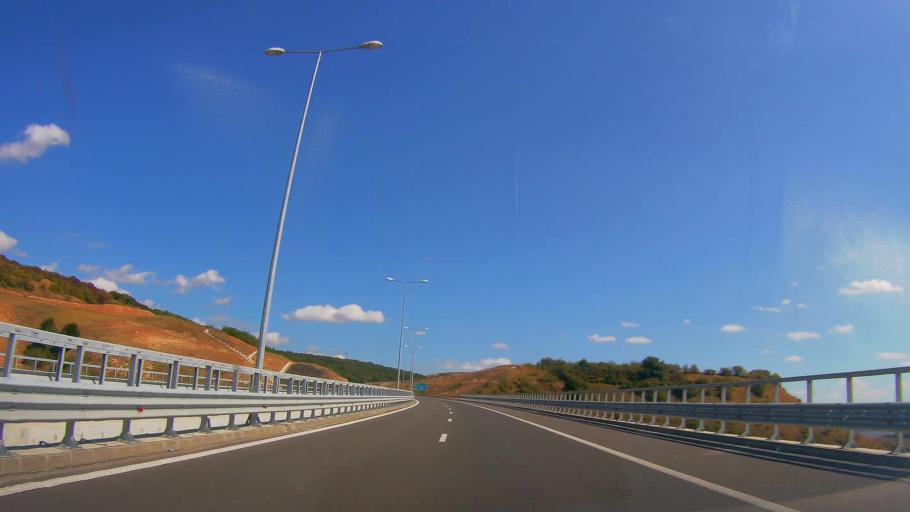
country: RO
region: Cluj
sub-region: Comuna Floresti
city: Luna de Sus
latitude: 46.7773
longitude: 23.4065
